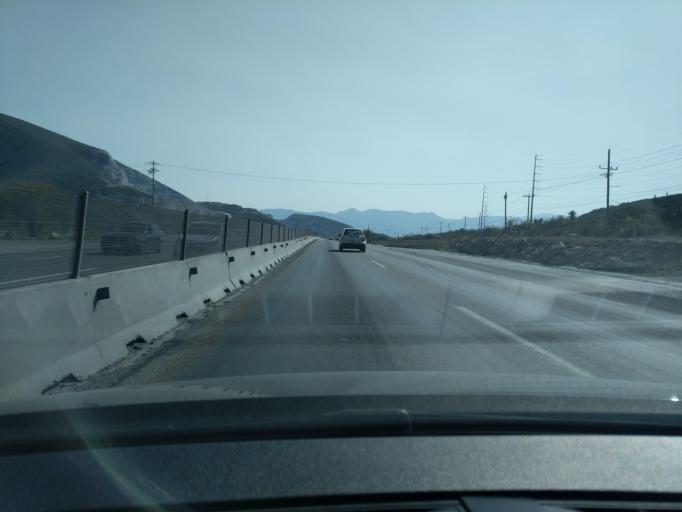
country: MX
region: Nuevo Leon
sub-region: Garcia
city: Los Parques
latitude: 25.7593
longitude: -100.4971
